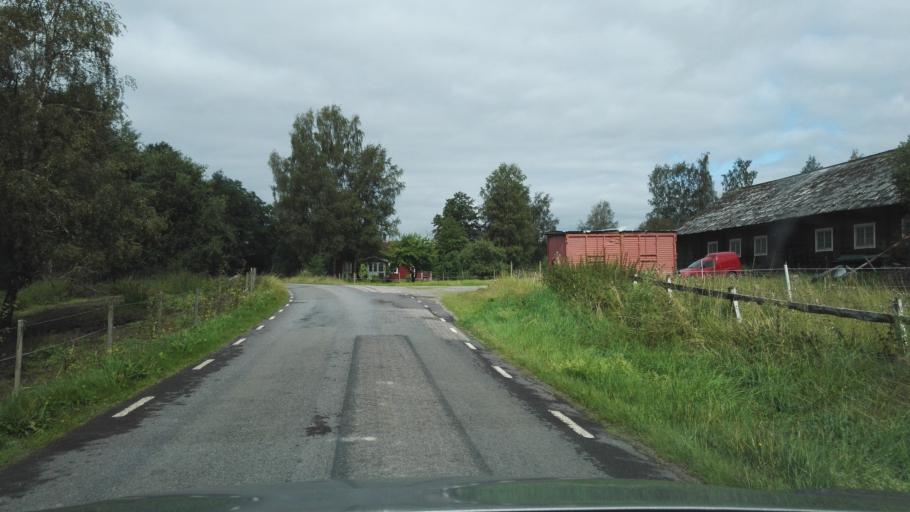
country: SE
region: Kronoberg
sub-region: Vaxjo Kommun
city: Rottne
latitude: 57.1701
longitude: 14.7898
